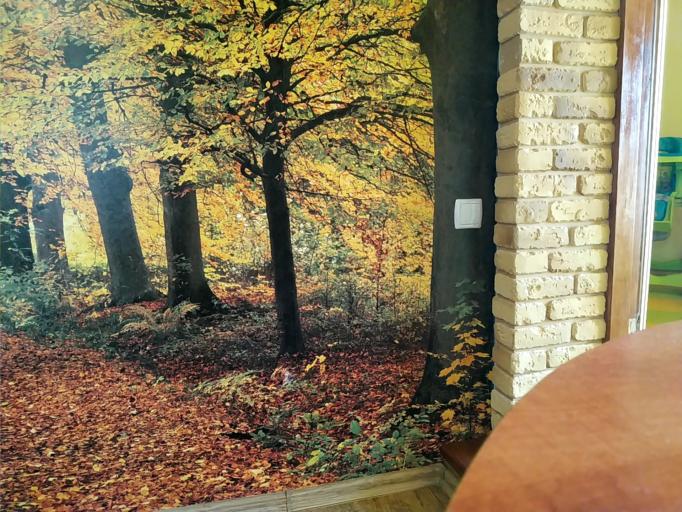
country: RU
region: Arkhangelskaya
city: Onega
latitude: 63.7470
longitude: 38.0783
